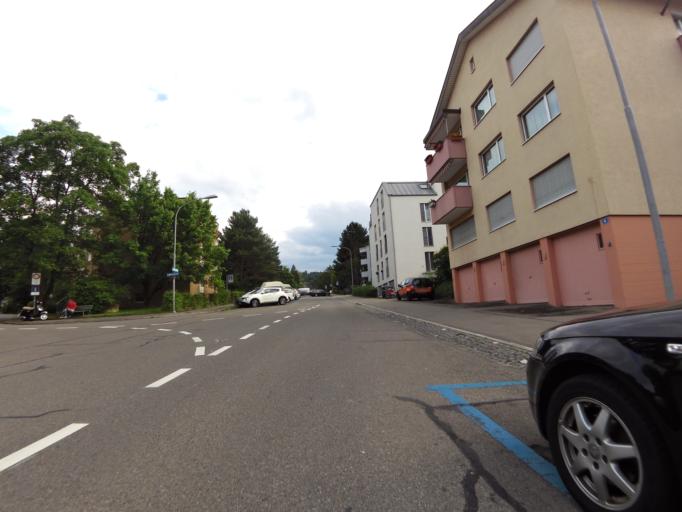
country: CH
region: Zurich
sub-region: Bezirk Zuerich
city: Zuerich (Kreis 9)
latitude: 47.3857
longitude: 8.4817
